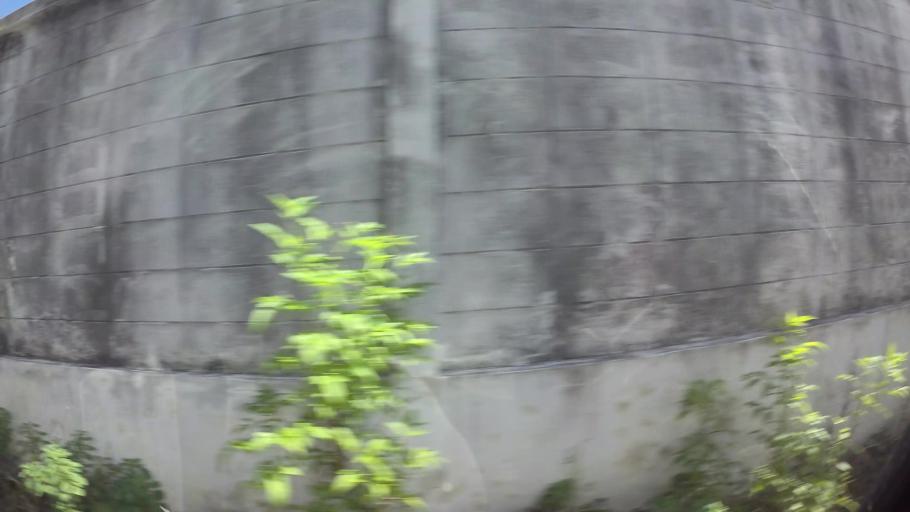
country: TH
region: Chon Buri
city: Phatthaya
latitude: 12.9481
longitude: 100.9018
